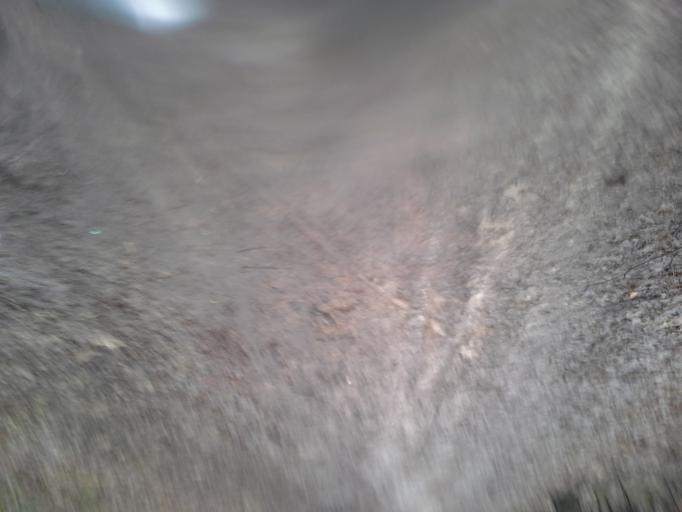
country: RU
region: Moscow
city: Yasenevo
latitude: 55.5764
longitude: 37.5364
